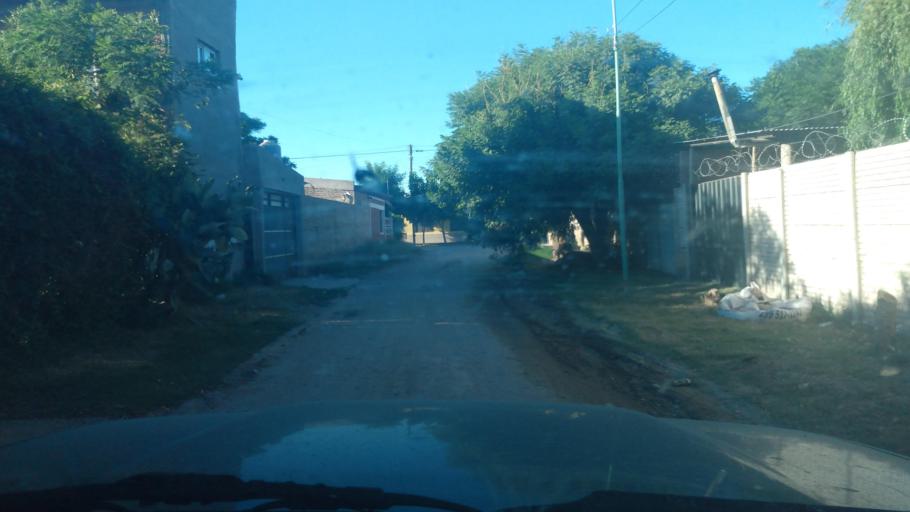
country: AR
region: Rio Negro
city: Catriel
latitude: -37.8705
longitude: -67.7899
